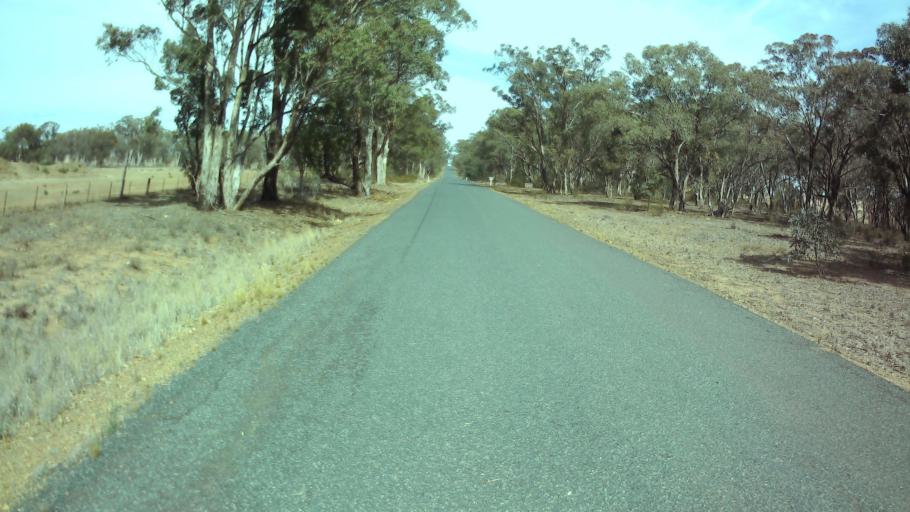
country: AU
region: New South Wales
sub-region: Weddin
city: Grenfell
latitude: -33.8073
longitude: 148.0548
